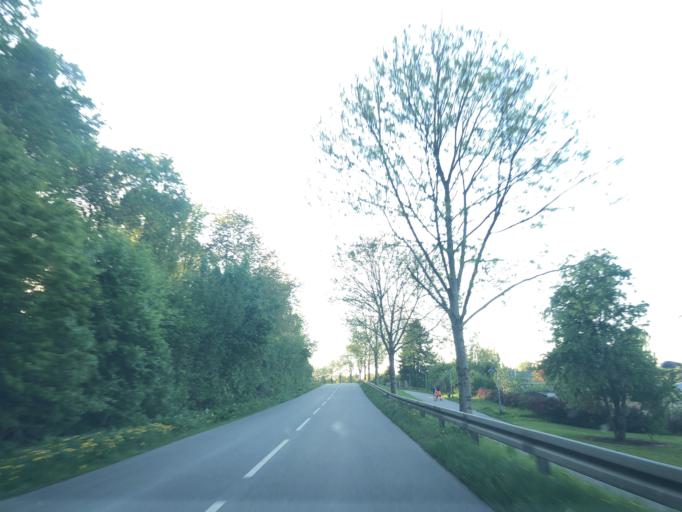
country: DK
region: Zealand
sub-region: Koge Kommune
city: Bjaeverskov
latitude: 55.4547
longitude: 12.0311
